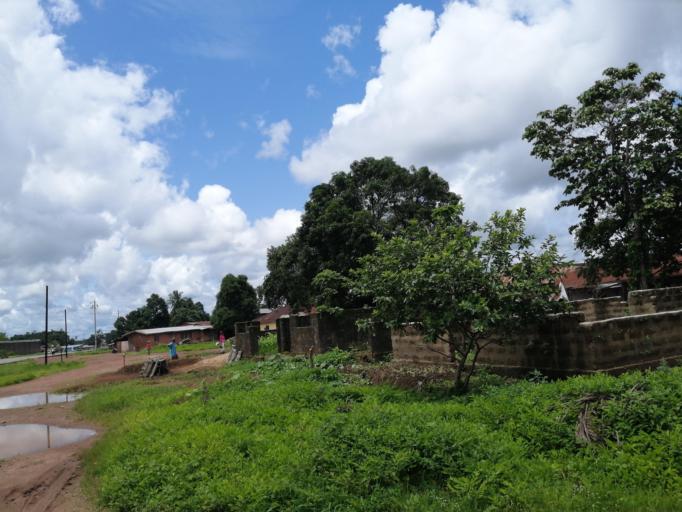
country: SL
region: Northern Province
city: Port Loko
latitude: 8.7748
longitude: -12.7913
